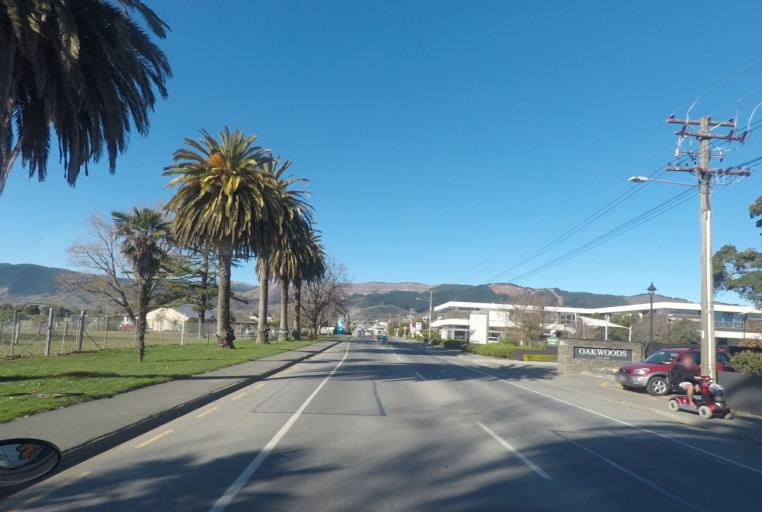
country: NZ
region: Tasman
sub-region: Tasman District
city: Richmond
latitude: -41.3342
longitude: 173.1792
